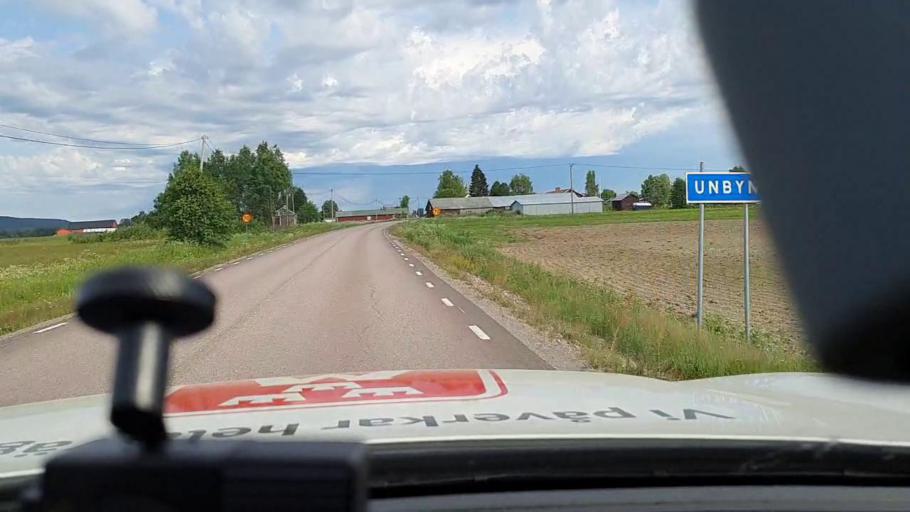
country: SE
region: Norrbotten
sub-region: Bodens Kommun
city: Saevast
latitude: 65.7014
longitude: 21.7706
